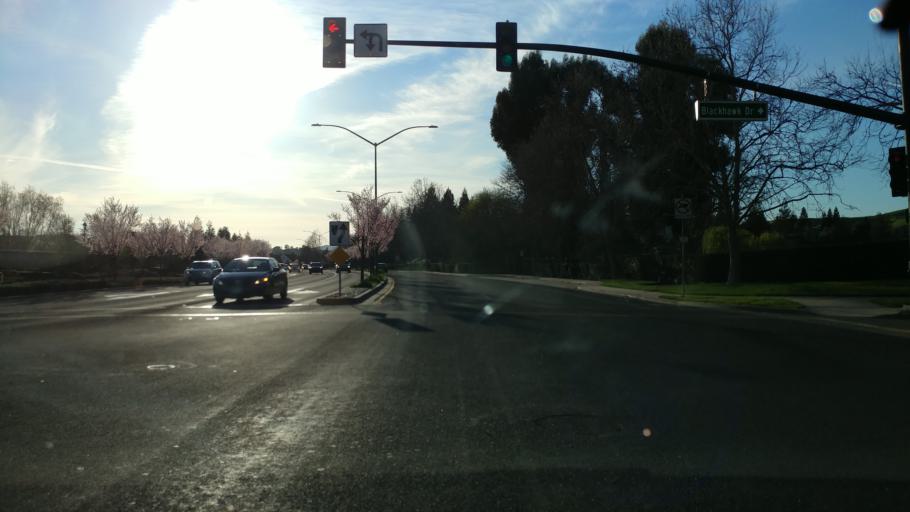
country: US
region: California
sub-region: Contra Costa County
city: Blackhawk
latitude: 37.7993
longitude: -121.8780
